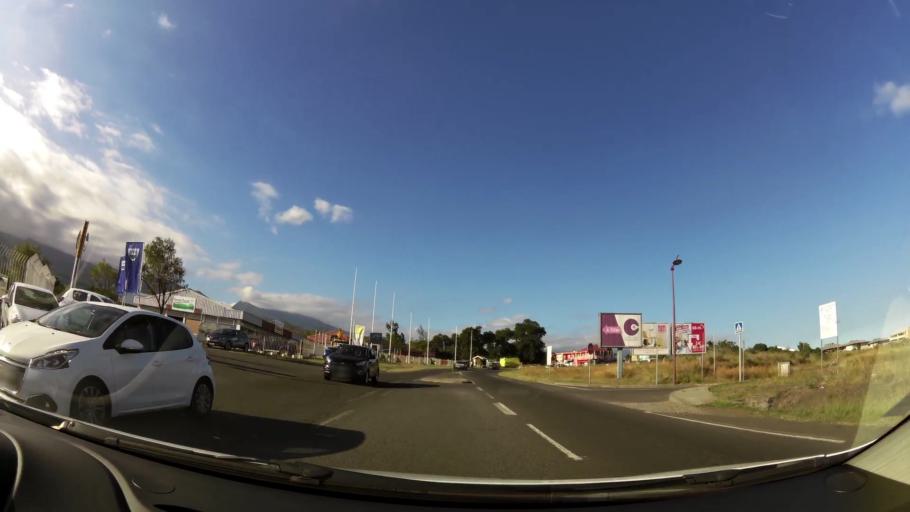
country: RE
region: Reunion
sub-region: Reunion
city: Saint-Louis
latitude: -21.2827
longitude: 55.4005
